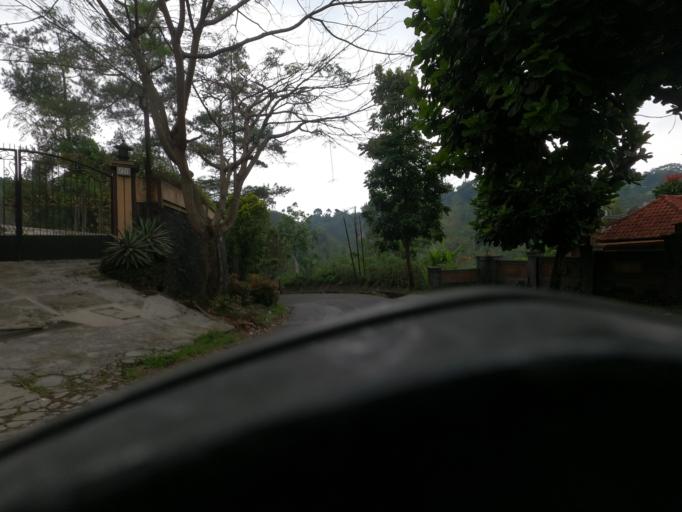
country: ID
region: West Java
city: Lembang
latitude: -6.8212
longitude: 107.6075
